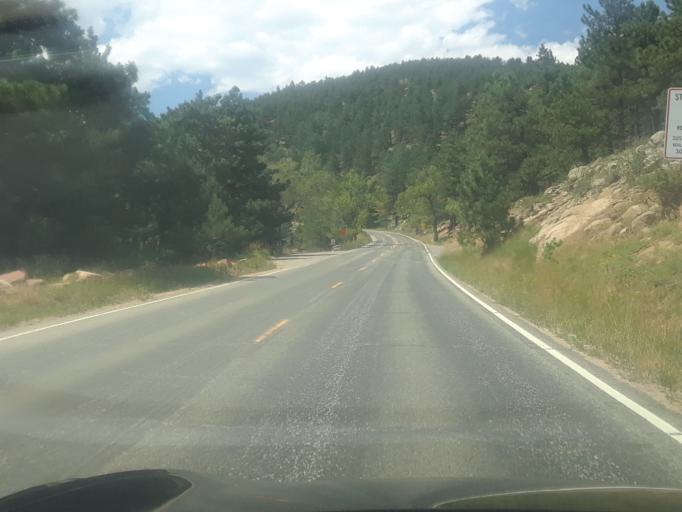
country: US
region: Colorado
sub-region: Boulder County
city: Boulder
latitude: 40.0343
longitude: -105.3242
